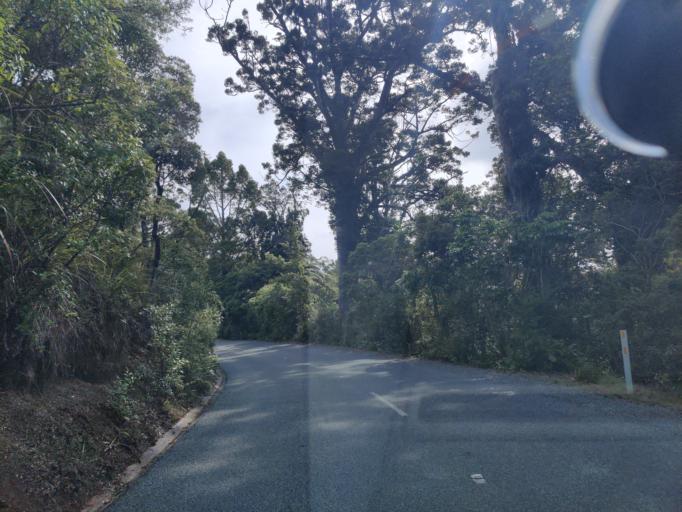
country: NZ
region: Northland
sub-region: Kaipara District
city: Dargaville
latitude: -35.6353
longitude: 173.5583
